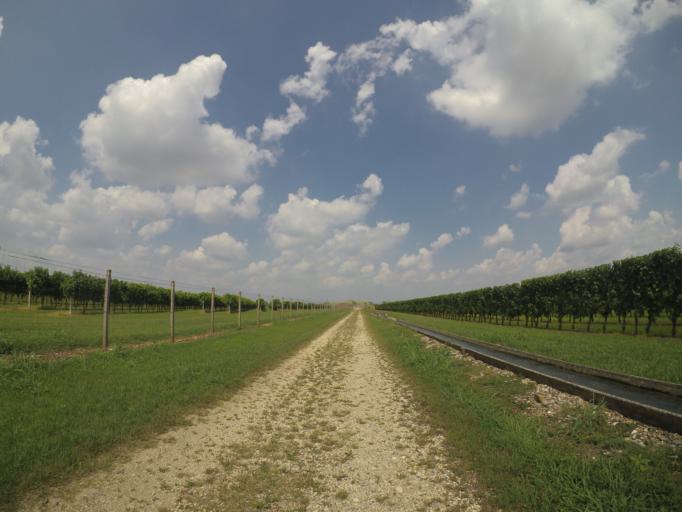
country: IT
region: Friuli Venezia Giulia
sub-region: Provincia di Udine
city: Bertiolo
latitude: 45.9668
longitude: 13.0385
